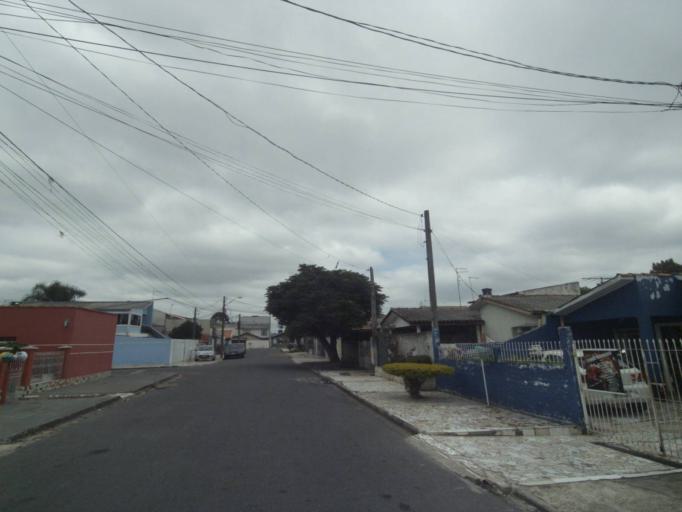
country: BR
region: Parana
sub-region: Sao Jose Dos Pinhais
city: Sao Jose dos Pinhais
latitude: -25.5349
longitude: -49.2613
